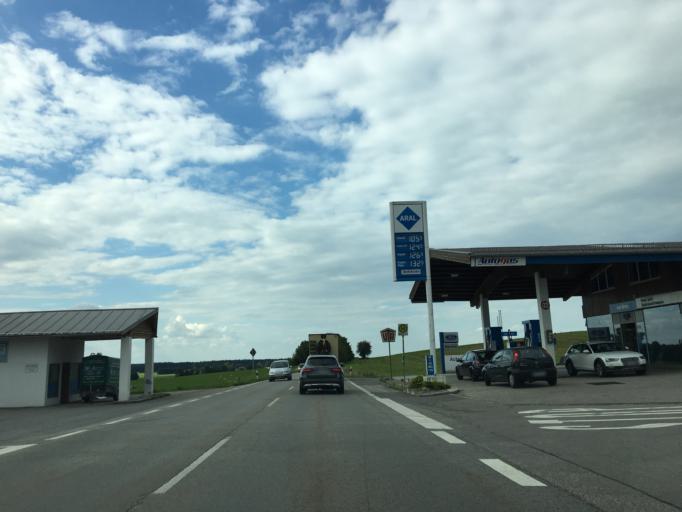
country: DE
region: Bavaria
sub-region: Upper Bavaria
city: Warngau
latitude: 47.8158
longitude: 11.7128
